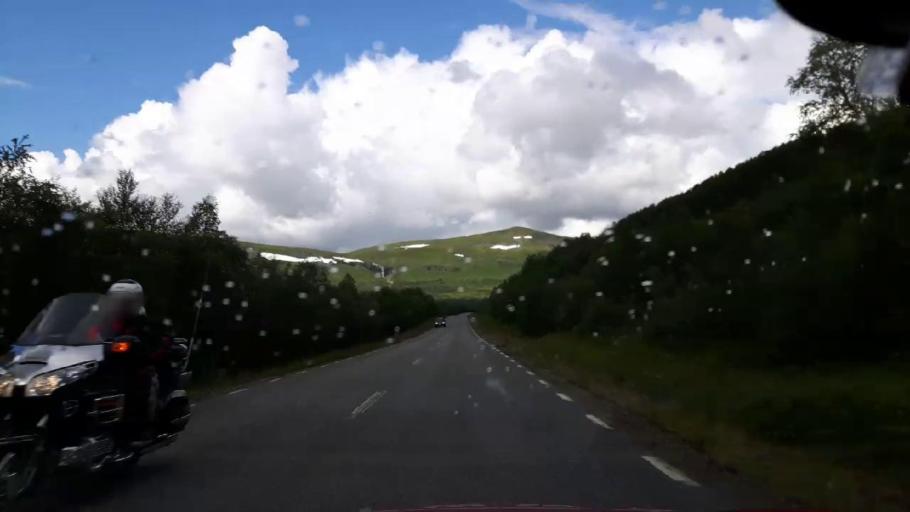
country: NO
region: Nordland
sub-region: Hattfjelldal
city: Hattfjelldal
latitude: 65.0682
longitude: 14.6749
